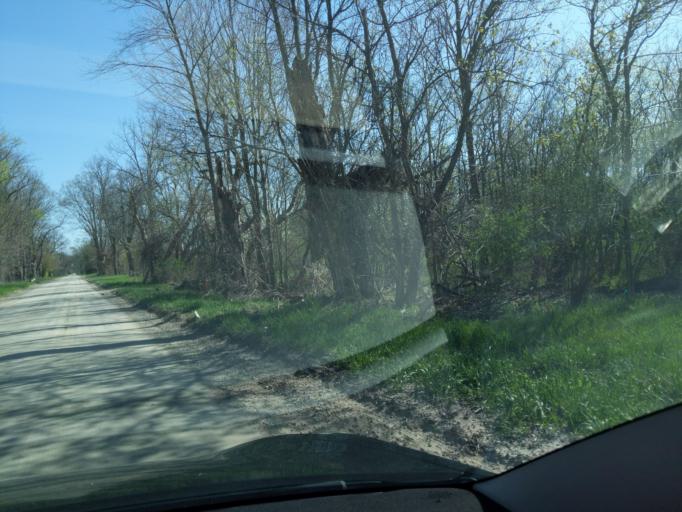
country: US
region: Michigan
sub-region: Ingham County
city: Stockbridge
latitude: 42.4157
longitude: -84.0836
